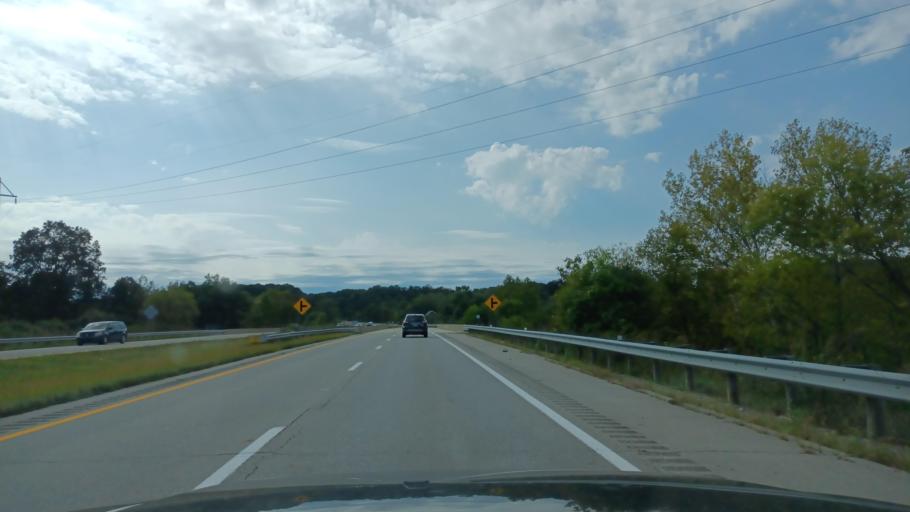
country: US
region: Ohio
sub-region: Athens County
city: Athens
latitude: 39.2878
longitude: -82.1378
